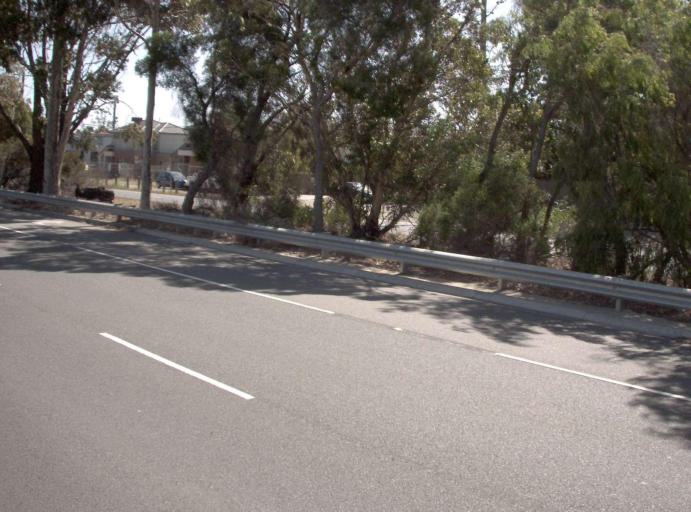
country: AU
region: Victoria
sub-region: Frankston
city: Frankston North
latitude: -38.1115
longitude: 145.1590
